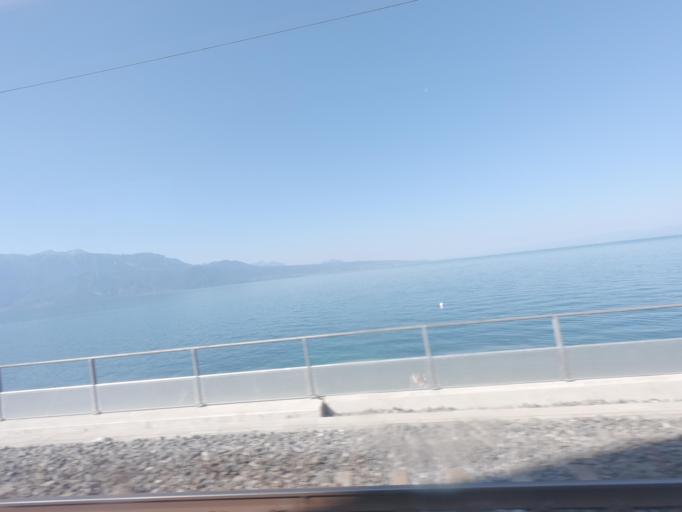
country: CH
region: Vaud
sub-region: Lavaux-Oron District
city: Cully
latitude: 46.4850
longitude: 6.7534
